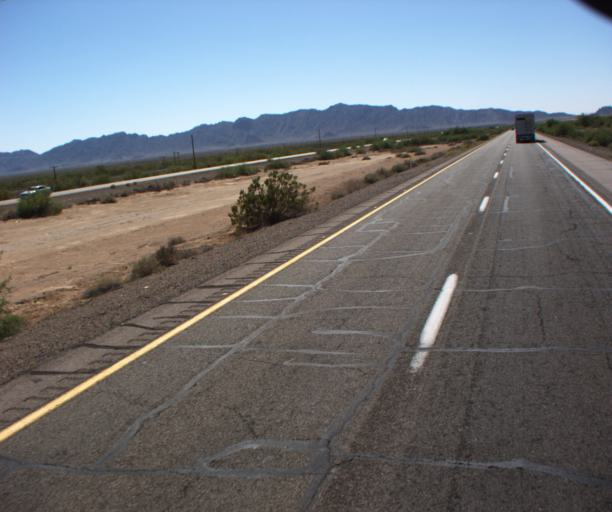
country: US
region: Arizona
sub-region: Yuma County
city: Wellton
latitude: 32.7546
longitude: -113.6524
